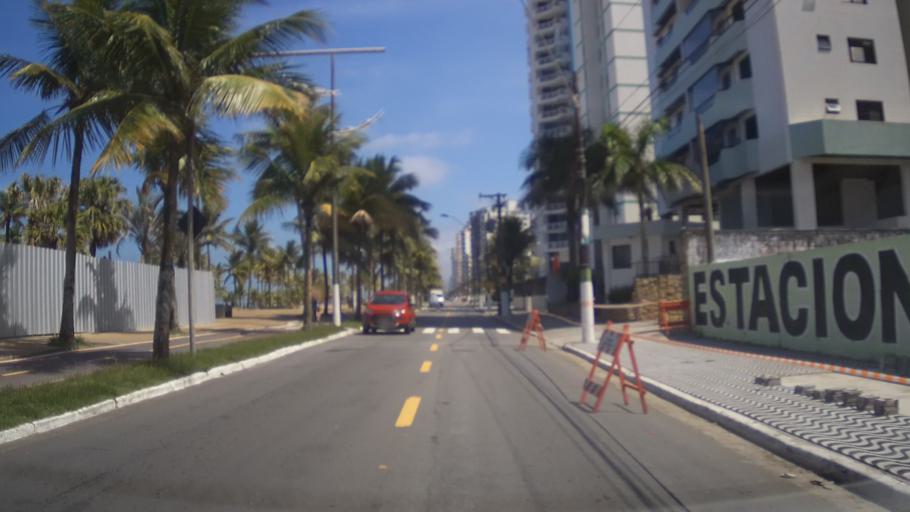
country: BR
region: Sao Paulo
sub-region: Praia Grande
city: Praia Grande
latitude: -24.0245
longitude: -46.4601
